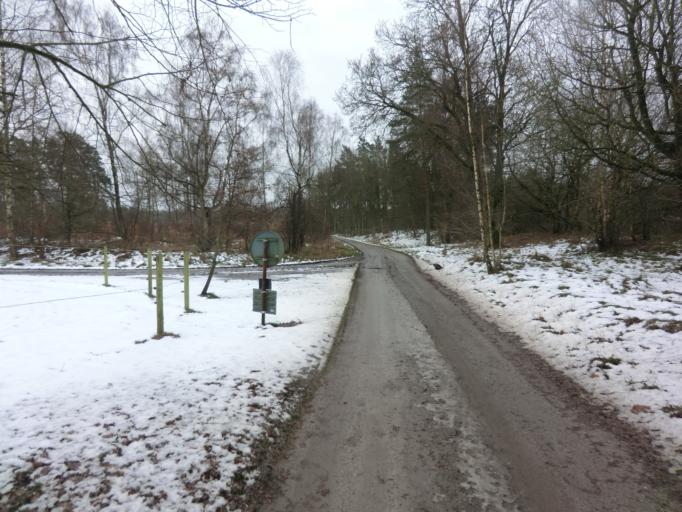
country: SE
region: Skane
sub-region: Hoors Kommun
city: Loberod
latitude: 55.7392
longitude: 13.3975
